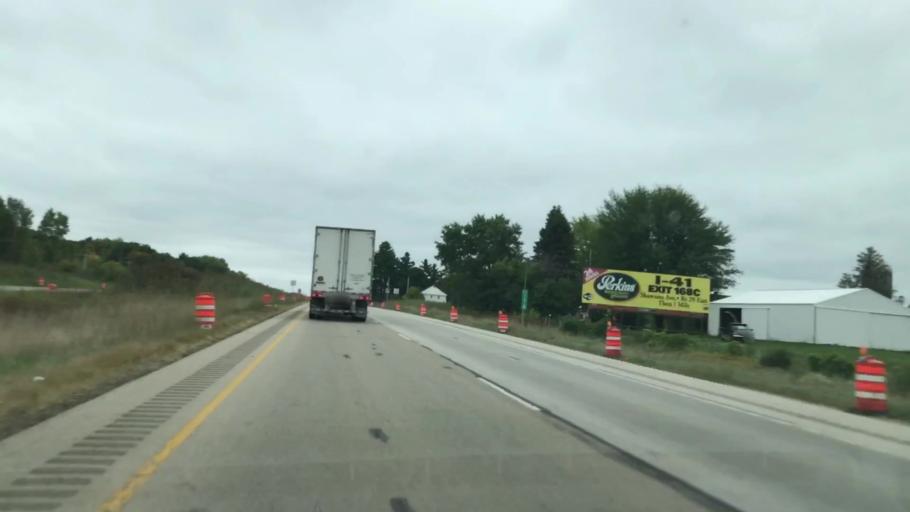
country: US
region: Wisconsin
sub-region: Brown County
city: Suamico
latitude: 44.6576
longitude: -88.0503
